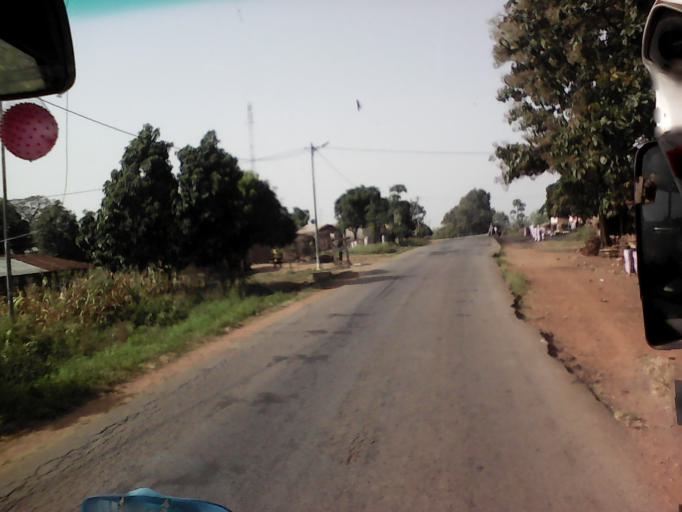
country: TG
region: Centrale
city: Sokode
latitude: 9.1384
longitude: 1.1534
